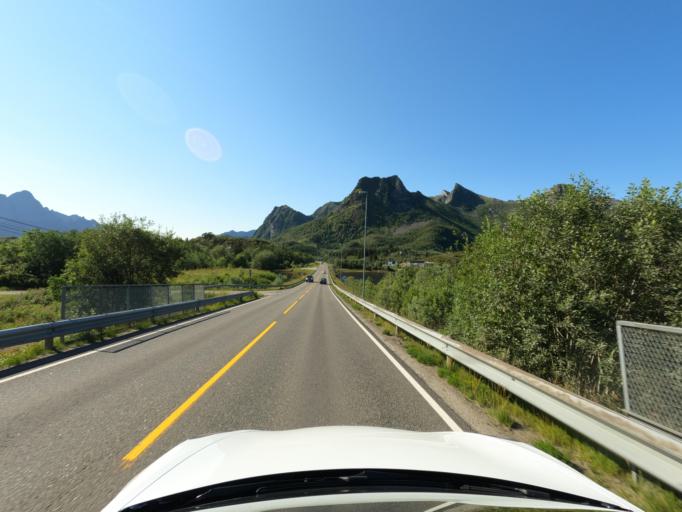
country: NO
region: Nordland
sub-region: Vagan
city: Kabelvag
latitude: 68.2147
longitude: 14.4453
